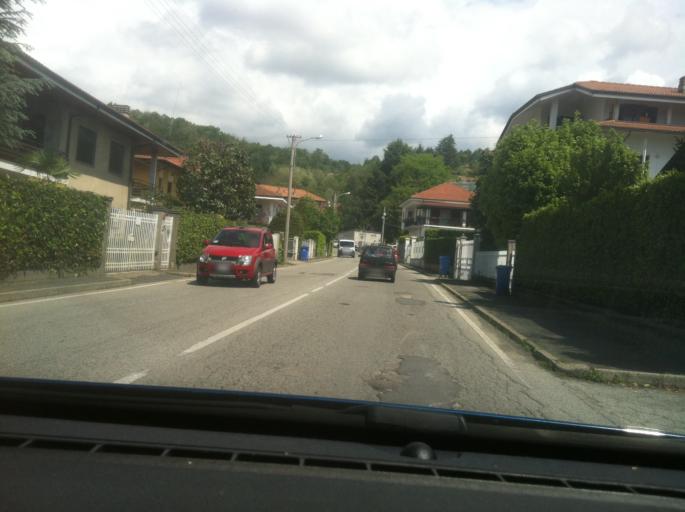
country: IT
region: Piedmont
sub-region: Provincia di Torino
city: Castellamonte
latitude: 45.3840
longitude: 7.7175
